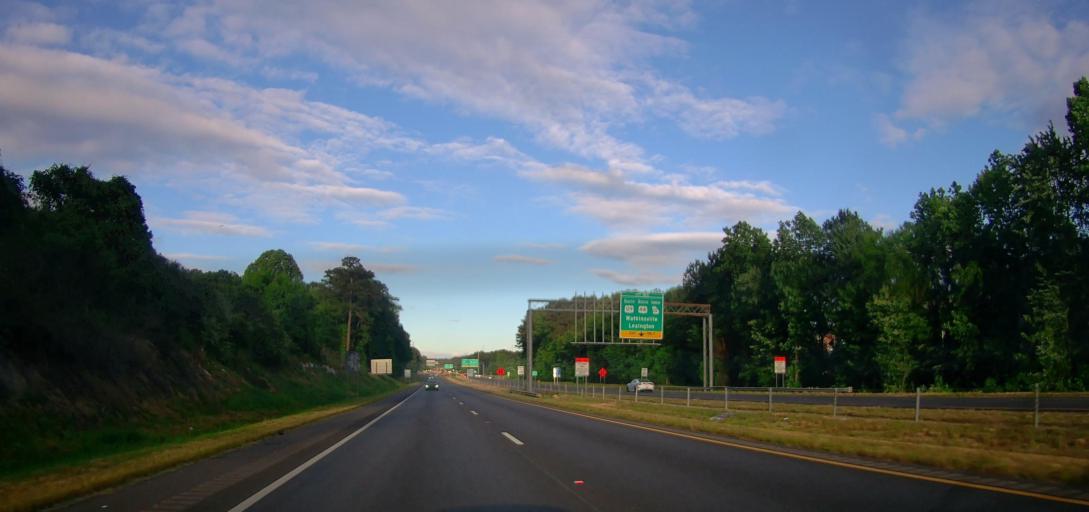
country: US
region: Georgia
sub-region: Clarke County
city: Athens
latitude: 33.9784
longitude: -83.3603
